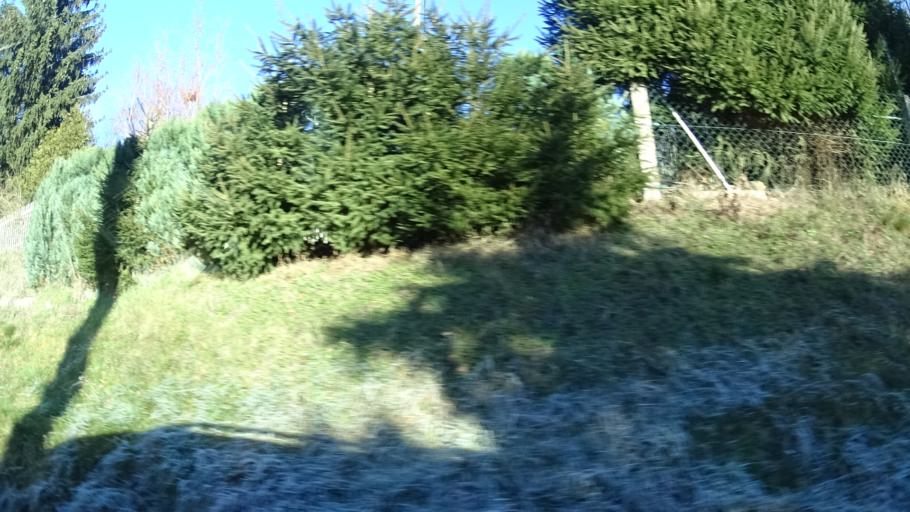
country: DE
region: Thuringia
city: Kleineutersdorf
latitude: 50.7890
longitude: 11.5853
